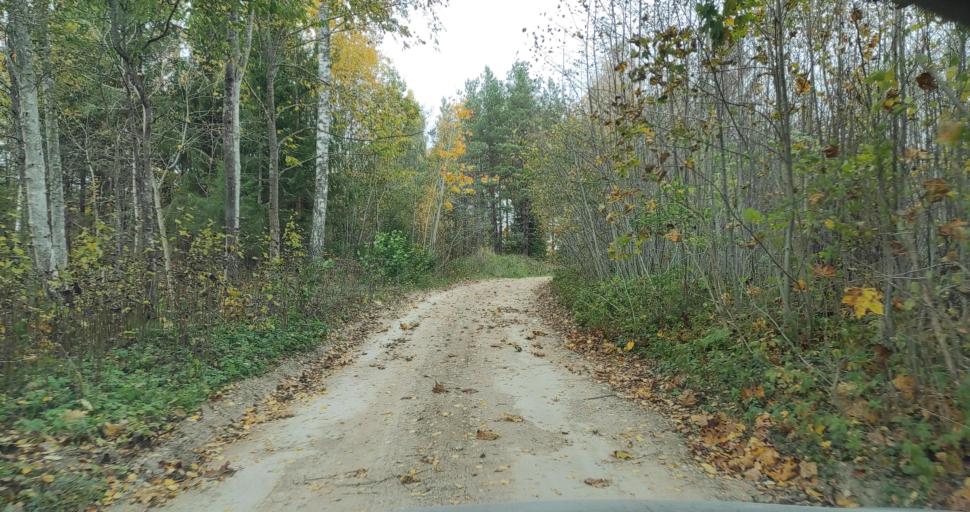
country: LV
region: Alsunga
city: Alsunga
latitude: 57.0369
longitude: 21.7121
